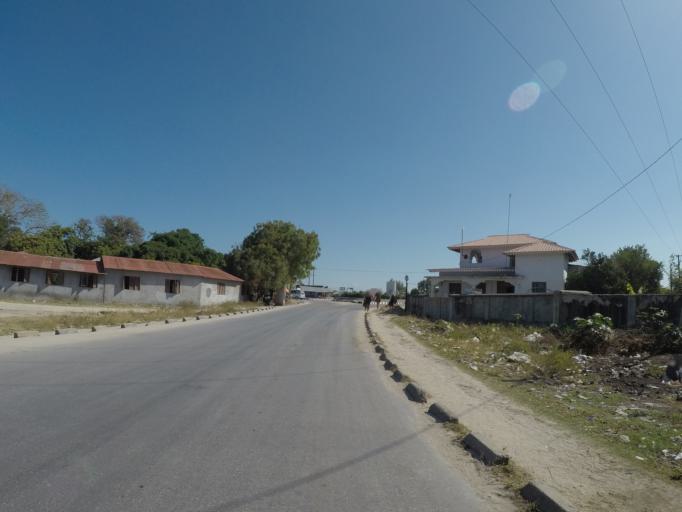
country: TZ
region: Zanzibar Central/South
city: Nganane
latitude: -6.2660
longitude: 39.5317
